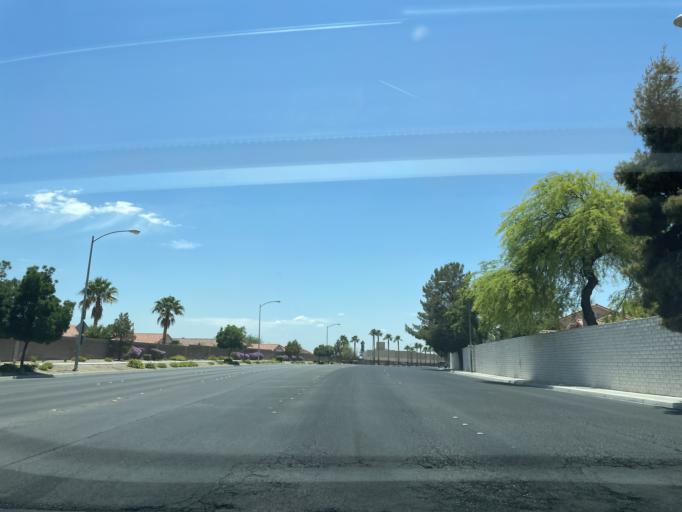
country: US
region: Nevada
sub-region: Clark County
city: North Las Vegas
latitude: 36.2656
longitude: -115.1532
